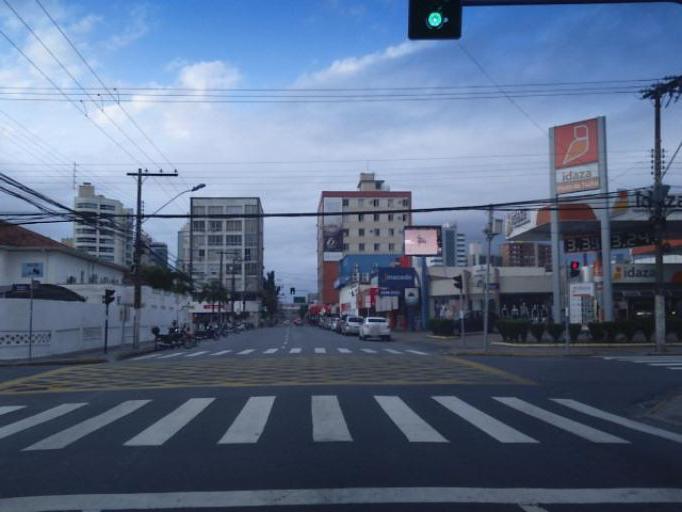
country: BR
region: Santa Catarina
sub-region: Itajai
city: Itajai
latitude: -26.9073
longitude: -48.6591
